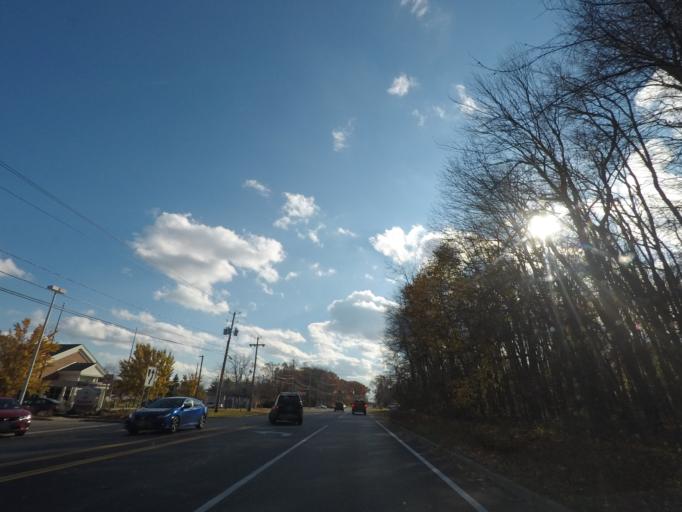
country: US
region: New York
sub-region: Schenectady County
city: Niskayuna
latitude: 42.7840
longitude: -73.8931
